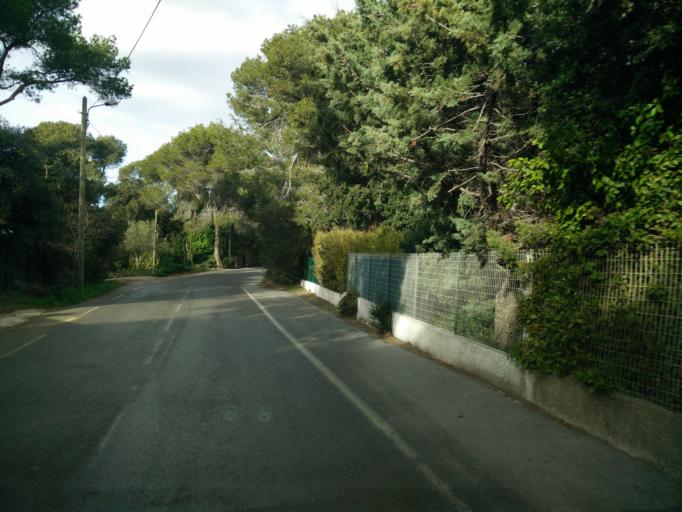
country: FR
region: Provence-Alpes-Cote d'Azur
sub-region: Departement du Var
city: Six-Fours-les-Plages
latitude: 43.0714
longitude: 5.8235
